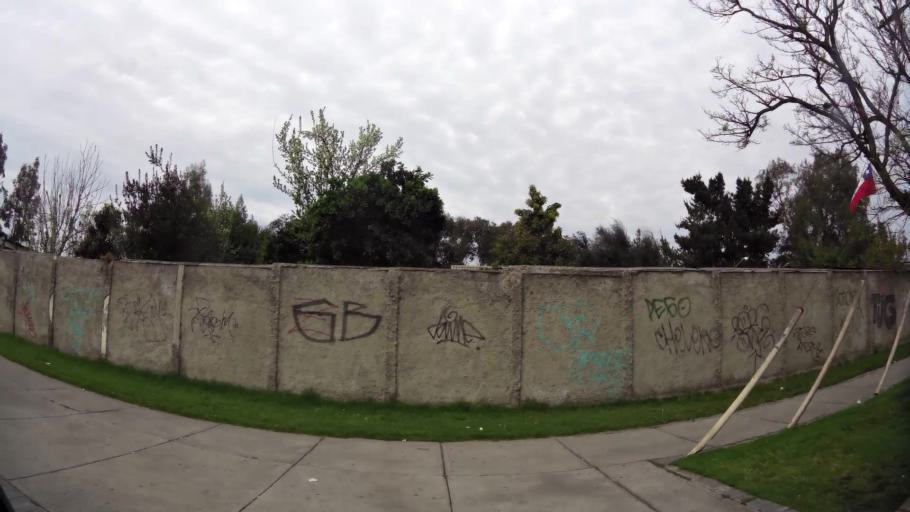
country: CL
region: Santiago Metropolitan
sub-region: Provincia de Santiago
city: Lo Prado
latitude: -33.5218
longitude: -70.7556
